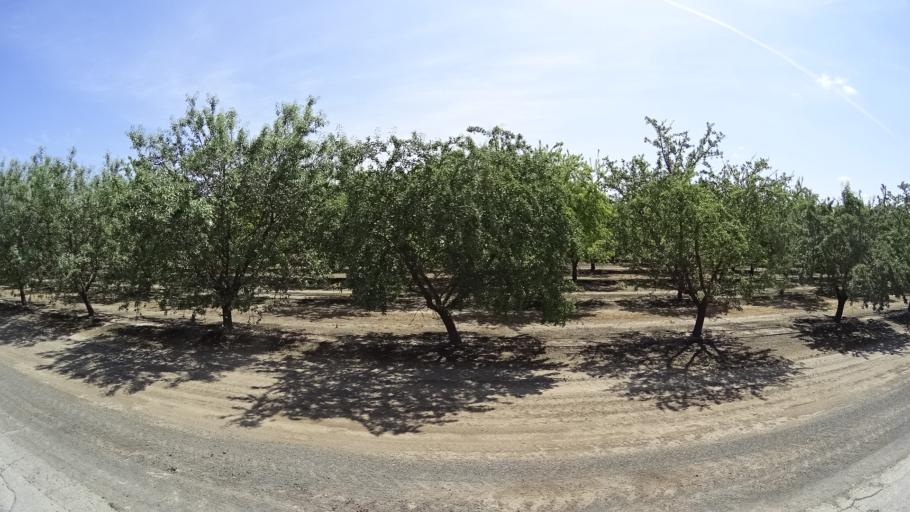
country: US
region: California
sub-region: Tulare County
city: Goshen
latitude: 36.2738
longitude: -119.4923
